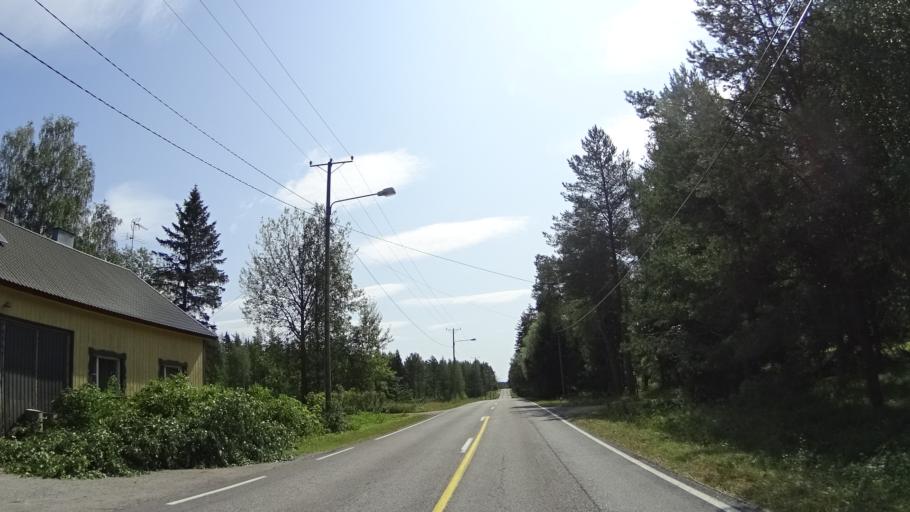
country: FI
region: Pirkanmaa
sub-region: Ylae-Pirkanmaa
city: Maenttae
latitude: 61.9057
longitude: 24.7875
